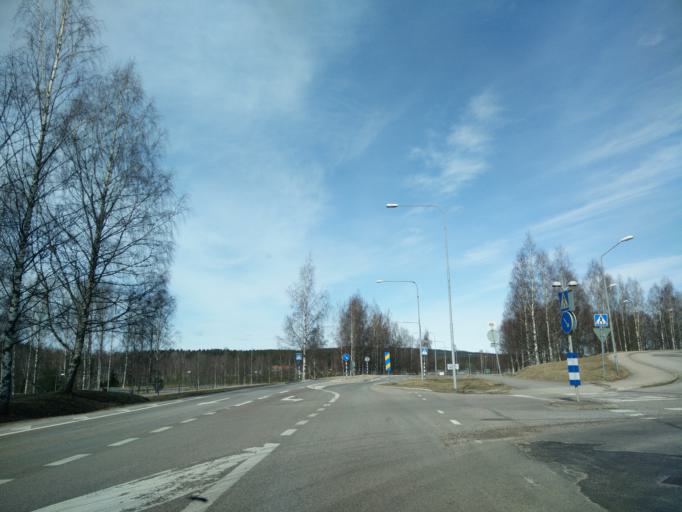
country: SE
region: Vaermland
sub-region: Hagfors Kommun
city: Hagfors
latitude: 60.0383
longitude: 13.7040
